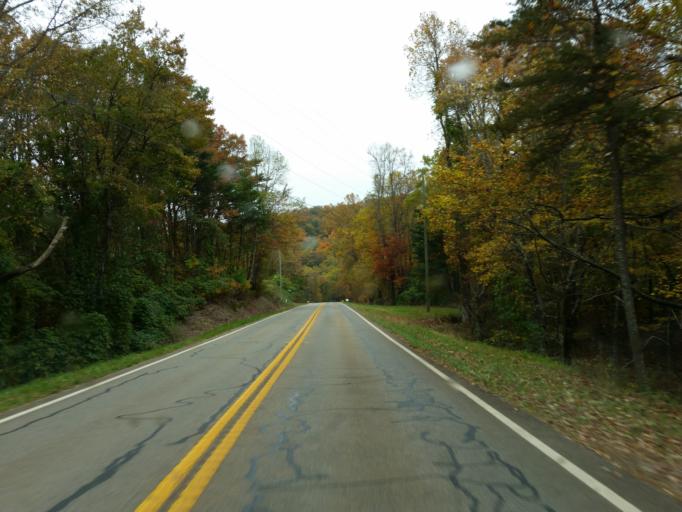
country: US
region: Georgia
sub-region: Pickens County
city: Jasper
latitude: 34.5306
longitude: -84.3934
